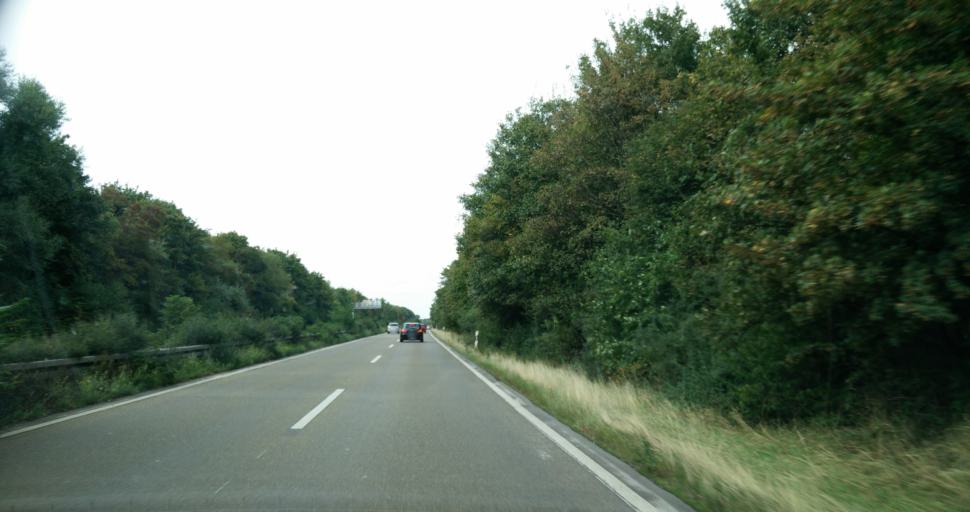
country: DE
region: North Rhine-Westphalia
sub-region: Regierungsbezirk Dusseldorf
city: Dusseldorf
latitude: 51.2799
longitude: 6.7452
